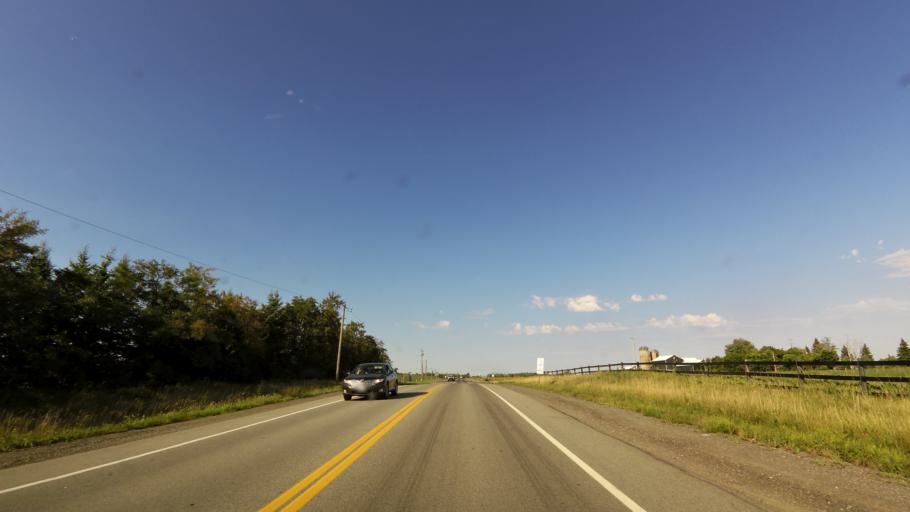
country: CA
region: Ontario
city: Brampton
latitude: 43.7430
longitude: -79.9118
